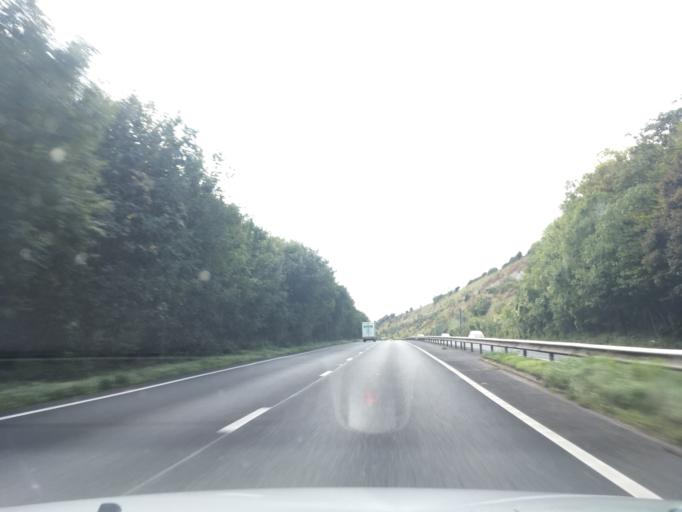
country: GB
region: England
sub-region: Hampshire
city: Petersfield
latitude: 50.9782
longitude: -0.9687
